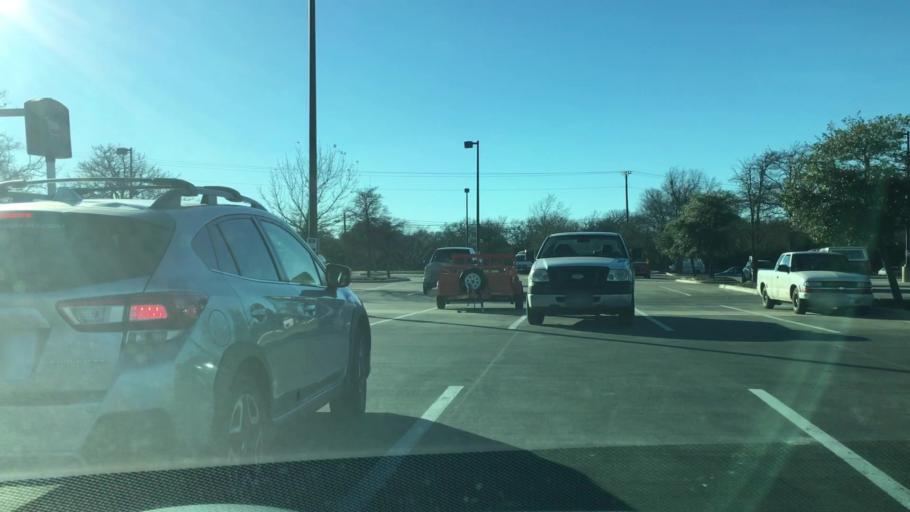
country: US
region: Texas
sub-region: Hays County
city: Dripping Springs
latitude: 30.1896
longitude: -98.0860
